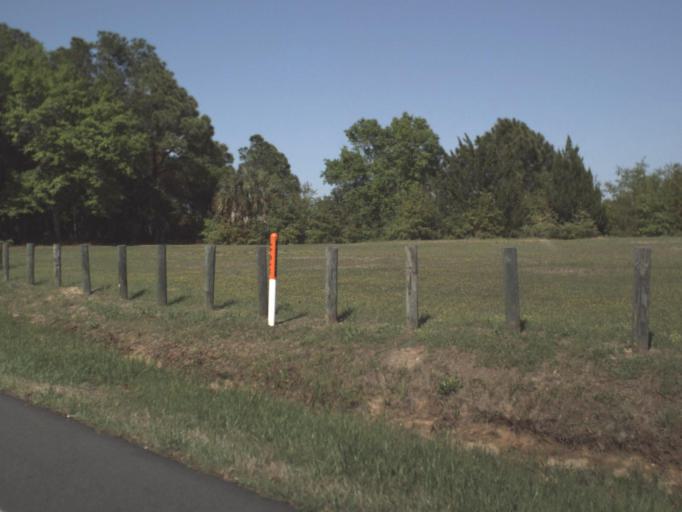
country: US
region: Florida
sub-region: Escambia County
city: East Pensacola Heights
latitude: 30.4472
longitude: -87.1728
